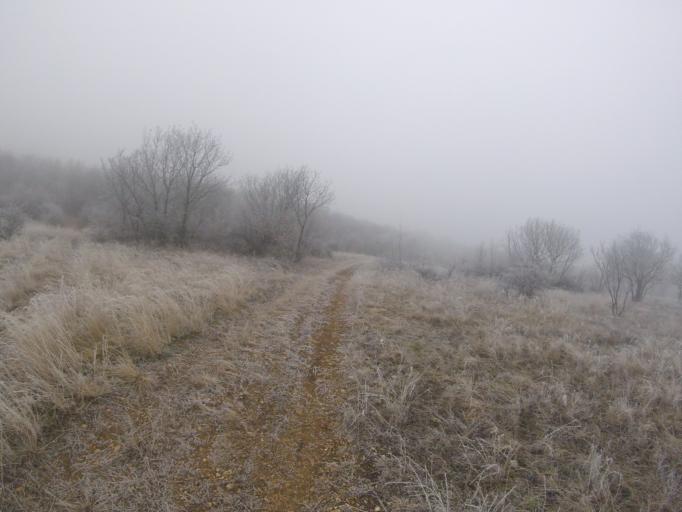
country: HU
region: Fejer
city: Csakvar
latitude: 47.3792
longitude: 18.4296
